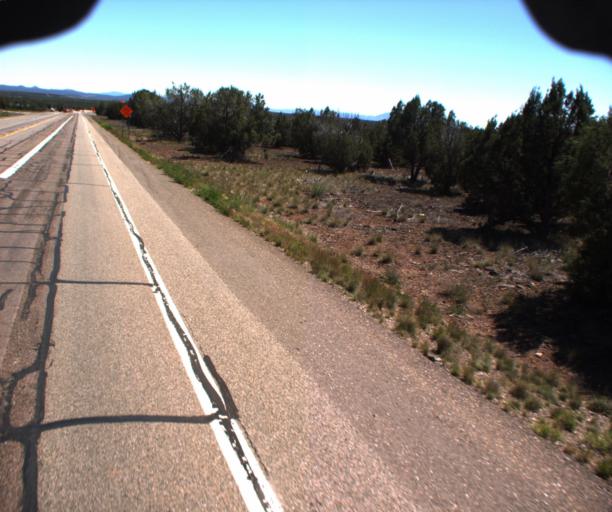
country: US
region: Arizona
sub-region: Yavapai County
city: Paulden
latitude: 35.0059
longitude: -112.3901
